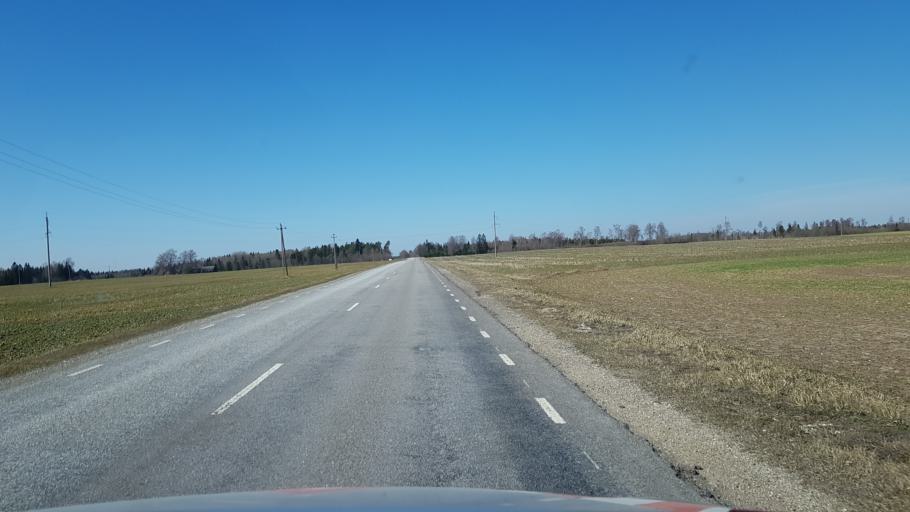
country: EE
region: Laeaene-Virumaa
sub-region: Vaeike-Maarja vald
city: Vaike-Maarja
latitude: 59.1469
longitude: 26.2281
